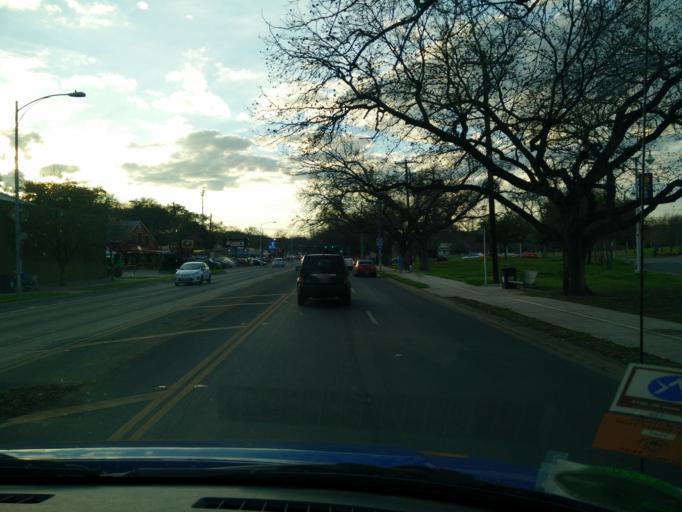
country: US
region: Texas
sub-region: Travis County
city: Austin
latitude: 30.2596
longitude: -97.7536
